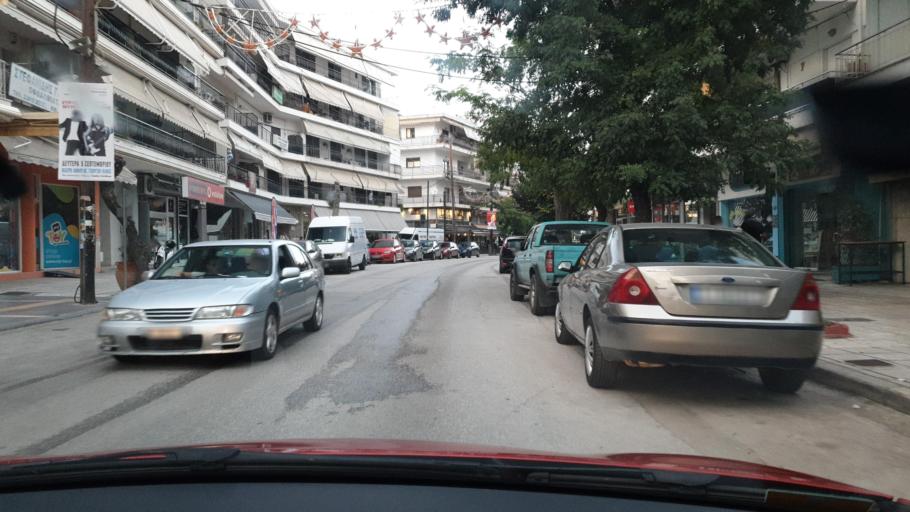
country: GR
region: Central Macedonia
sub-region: Nomos Kilkis
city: Kilkis
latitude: 40.9913
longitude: 22.8714
